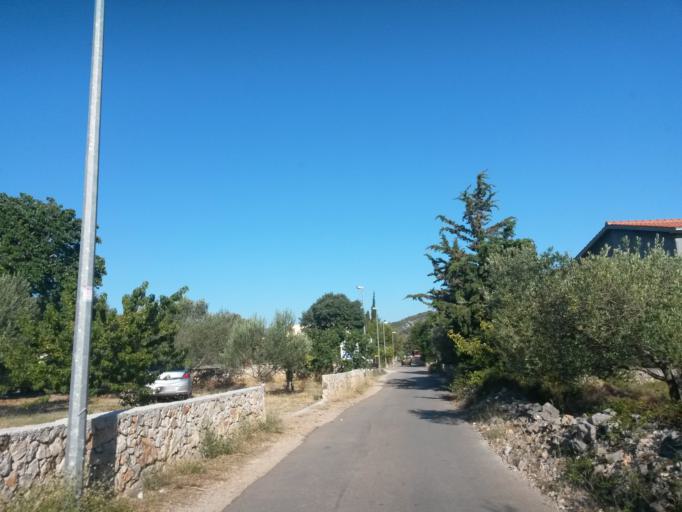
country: HR
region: Sibensko-Kniniska
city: Rogoznica
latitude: 43.5426
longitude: 15.9581
